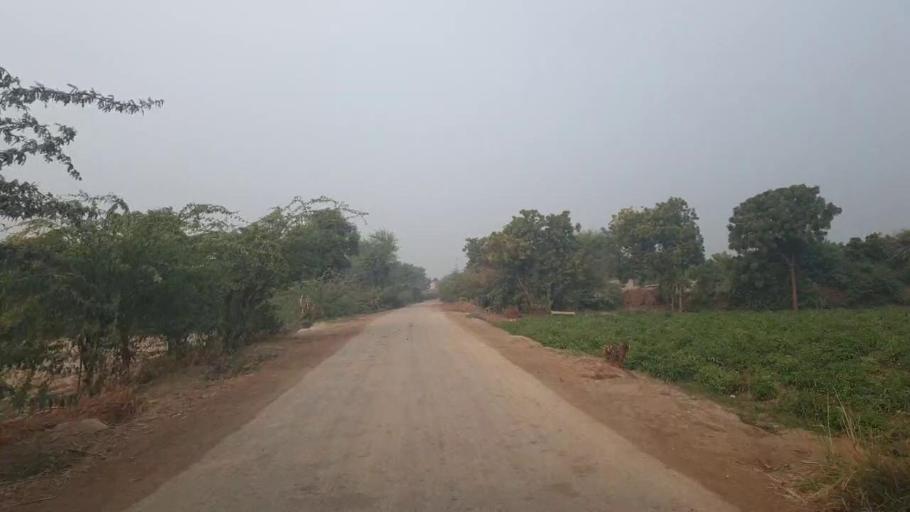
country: PK
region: Sindh
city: Tando Adam
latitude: 25.7101
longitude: 68.6488
